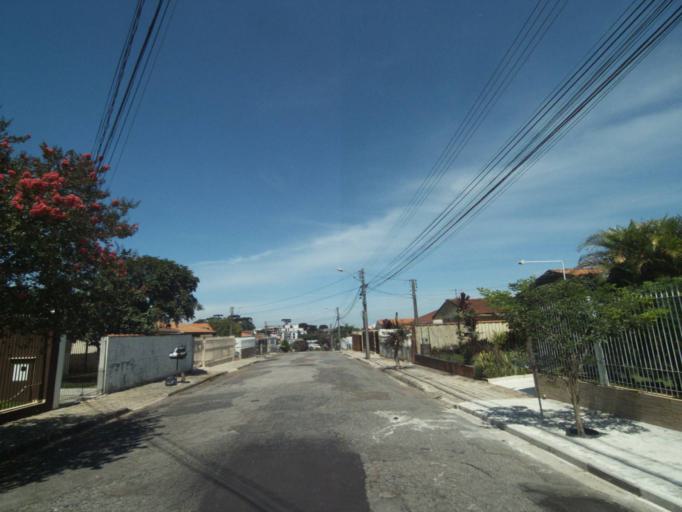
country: BR
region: Parana
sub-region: Curitiba
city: Curitiba
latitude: -25.4641
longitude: -49.2395
